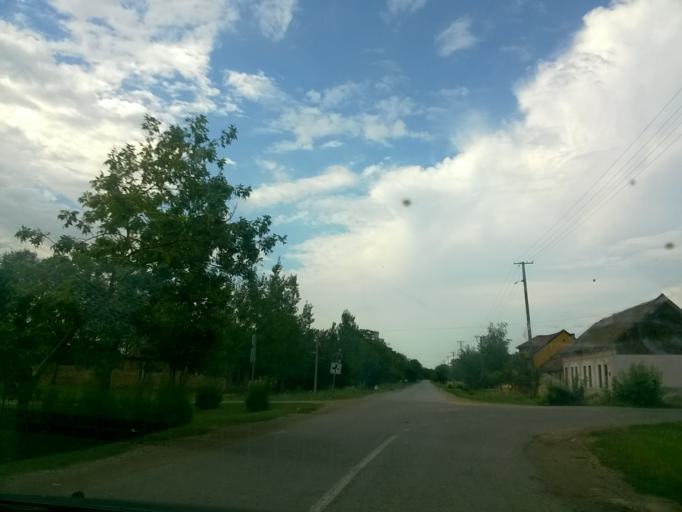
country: RS
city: Orlovat
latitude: 45.2480
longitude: 20.5852
